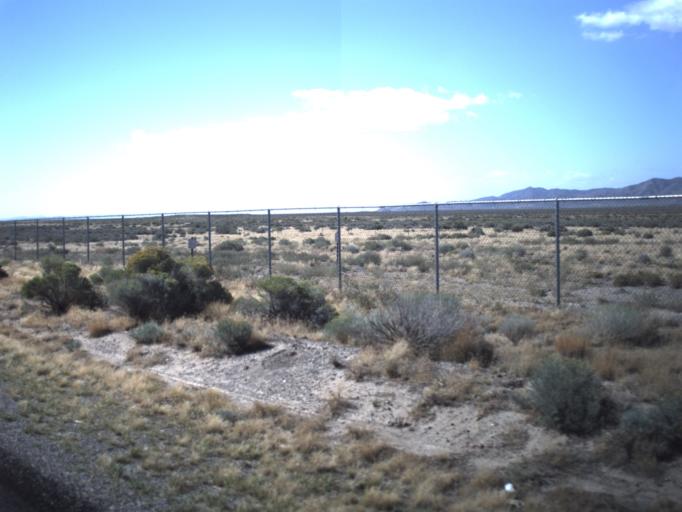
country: US
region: Utah
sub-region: Beaver County
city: Milford
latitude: 38.4332
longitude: -113.0098
